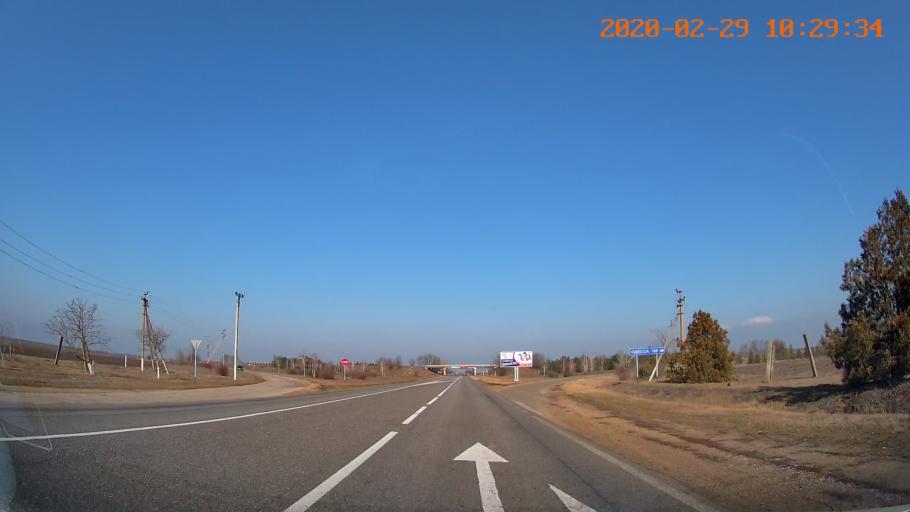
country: MD
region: Telenesti
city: Tiraspolul Nou
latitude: 46.9251
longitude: 29.5843
